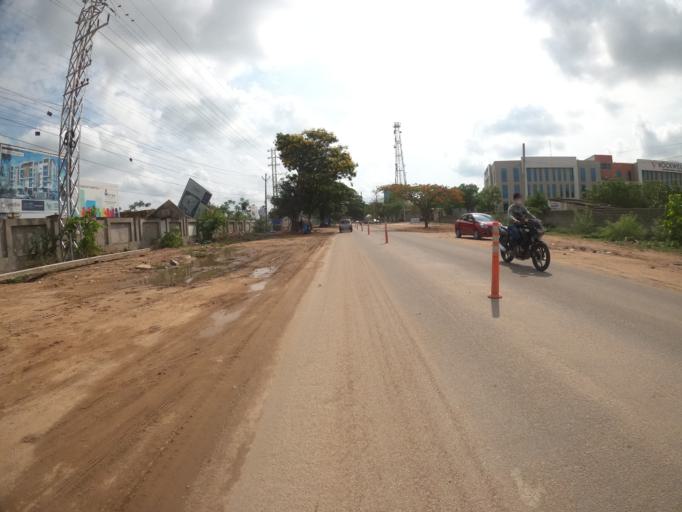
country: IN
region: Telangana
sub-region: Medak
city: Serilingampalle
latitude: 17.3861
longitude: 78.3354
